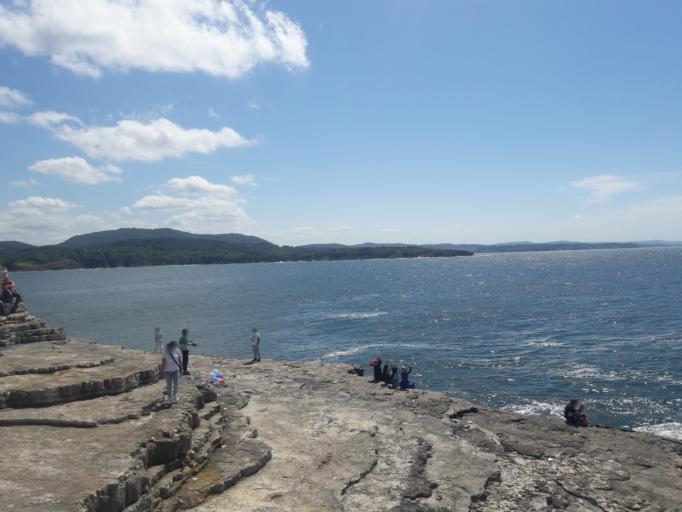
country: TR
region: Kocaeli
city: Kandira
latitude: 41.1589
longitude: 30.1912
